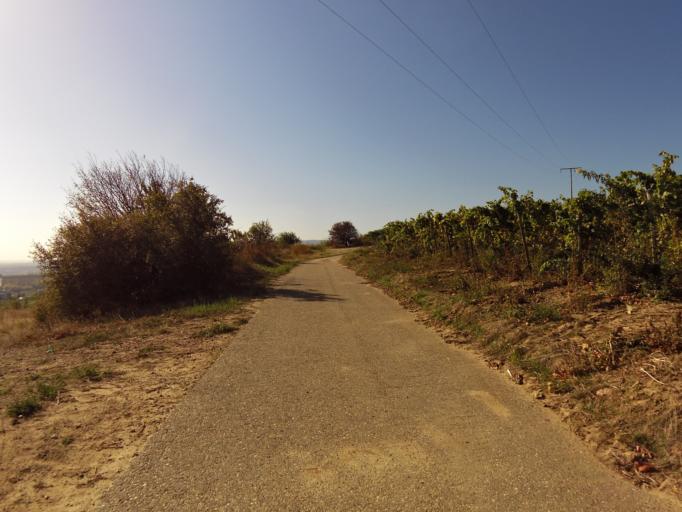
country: DE
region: Rheinland-Pfalz
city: Kallstadt
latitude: 49.4989
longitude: 8.1705
